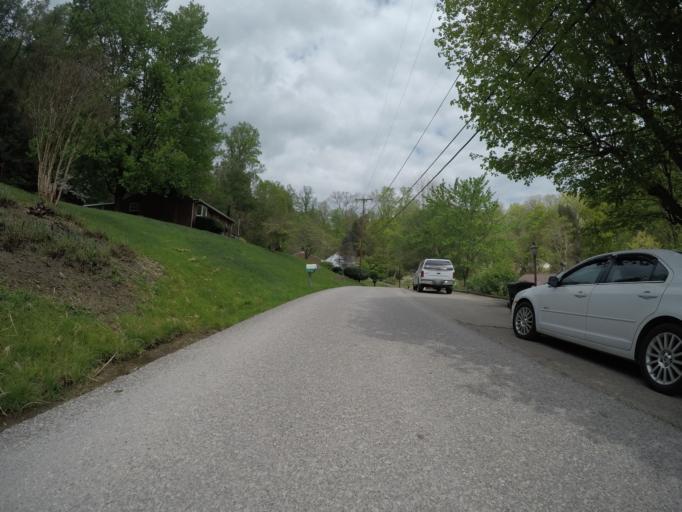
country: US
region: West Virginia
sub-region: Kanawha County
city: Charleston
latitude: 38.3889
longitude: -81.6065
